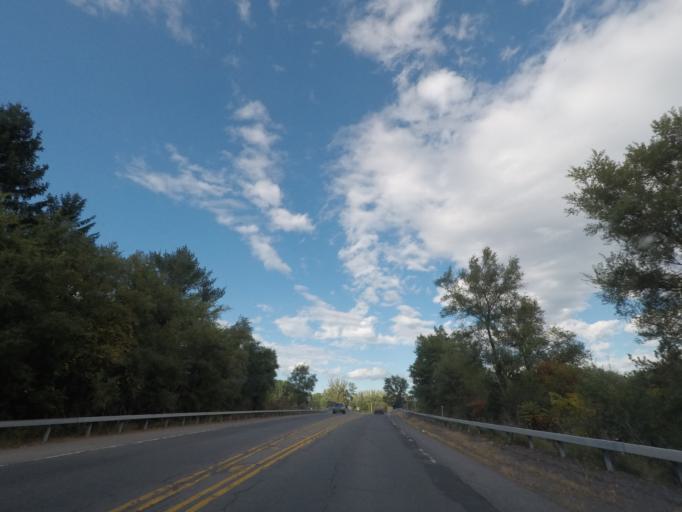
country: US
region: New York
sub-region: Schenectady County
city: Rotterdam
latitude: 42.7576
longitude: -73.9436
